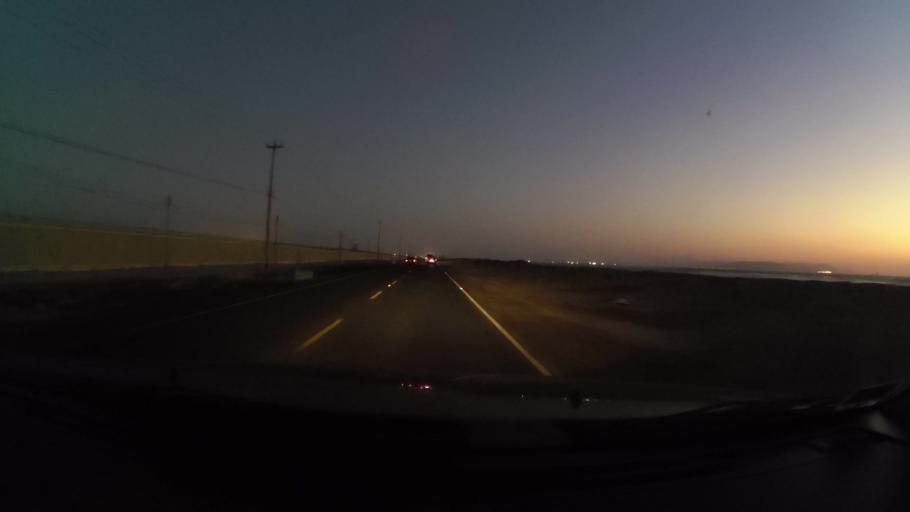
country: PE
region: Ica
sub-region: Provincia de Pisco
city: Pisco
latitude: -13.7540
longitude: -76.2306
